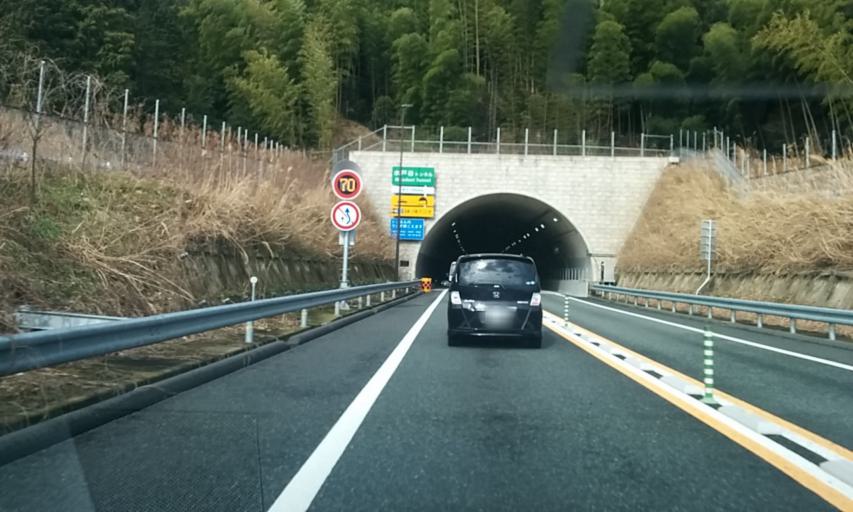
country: JP
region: Kyoto
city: Miyazu
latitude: 35.5529
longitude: 135.1337
